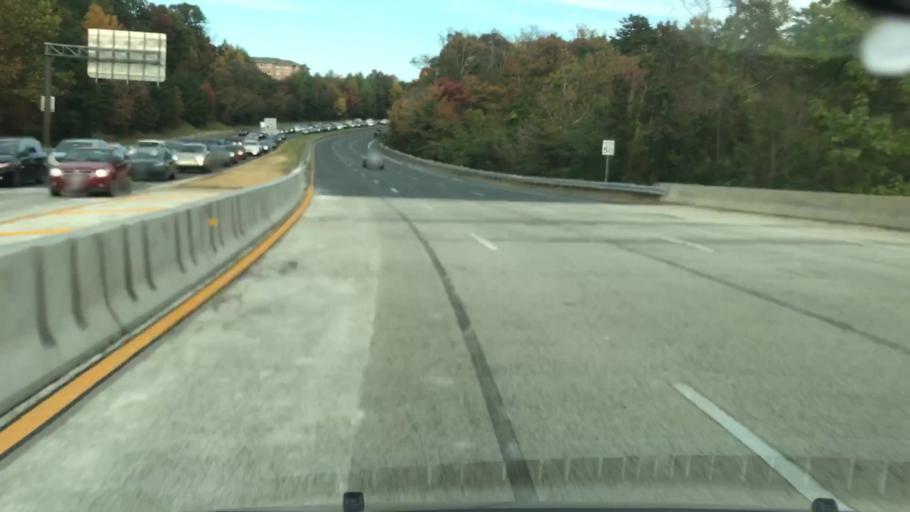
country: US
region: Virginia
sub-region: Fairfax County
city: West Springfield
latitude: 38.7620
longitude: -77.2080
